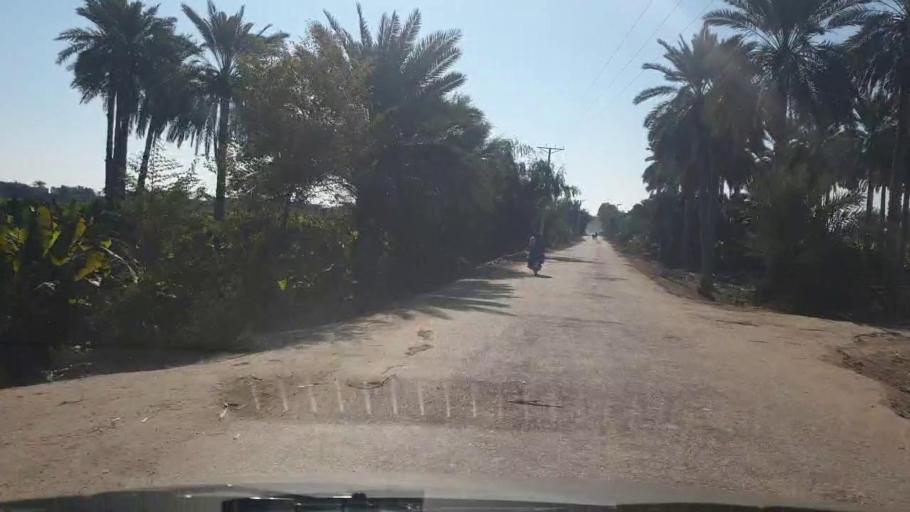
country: PK
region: Sindh
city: Bozdar
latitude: 27.2486
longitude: 68.6519
